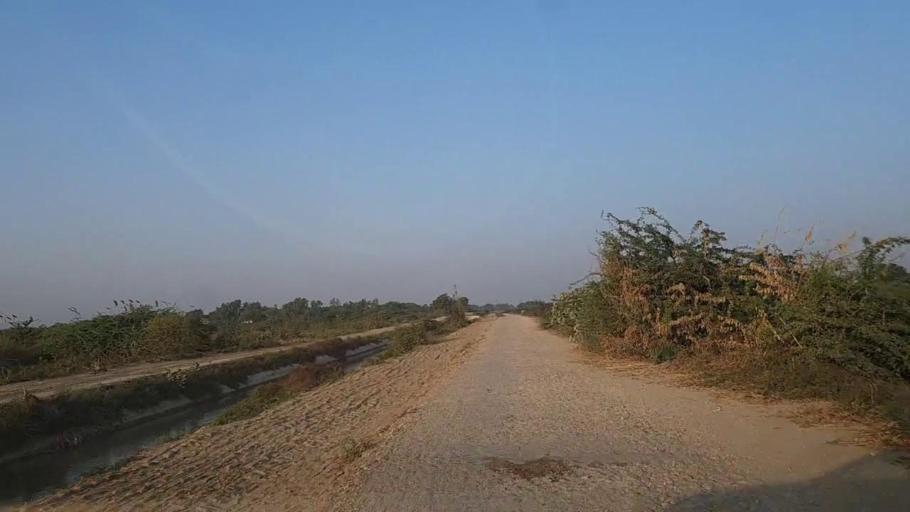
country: PK
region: Sindh
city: Mirpur Sakro
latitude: 24.2848
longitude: 67.6898
